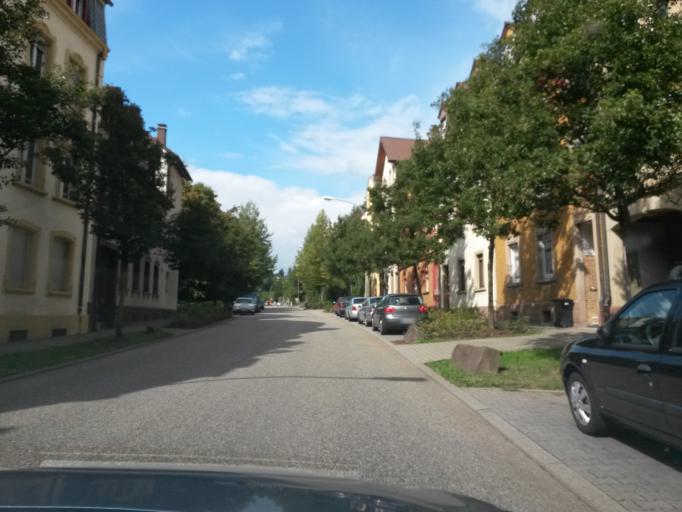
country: DE
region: Baden-Wuerttemberg
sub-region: Karlsruhe Region
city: Ispringen
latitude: 48.8920
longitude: 8.6634
